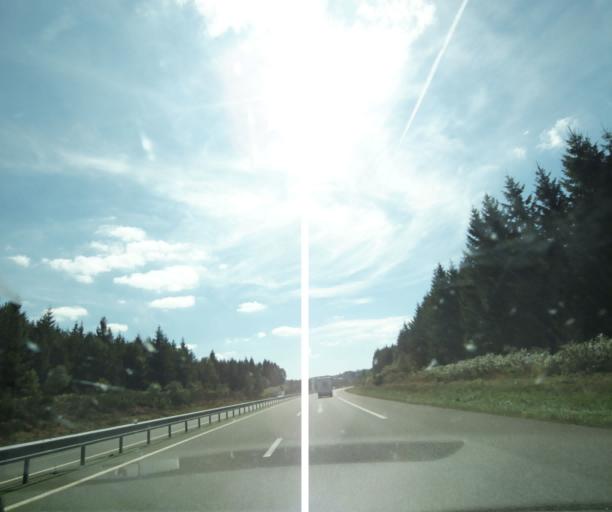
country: FR
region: Auvergne
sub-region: Departement du Puy-de-Dome
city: Saint-Sauves-d'Auvergne
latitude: 45.6859
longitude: 2.6962
